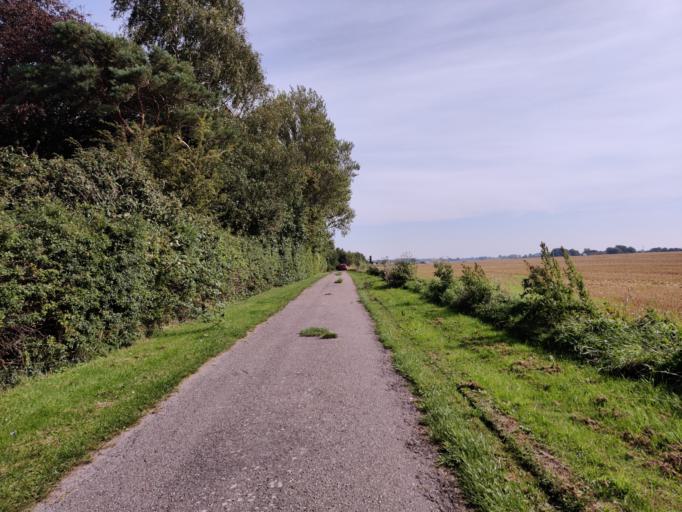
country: DK
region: Zealand
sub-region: Guldborgsund Kommune
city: Nykobing Falster
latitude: 54.6322
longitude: 11.9073
